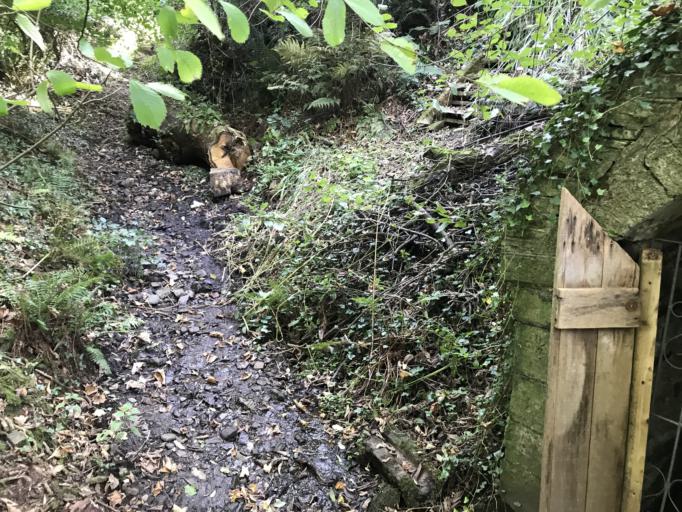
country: GB
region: England
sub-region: Cornwall
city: Flexbury
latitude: 50.9945
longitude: -4.5147
